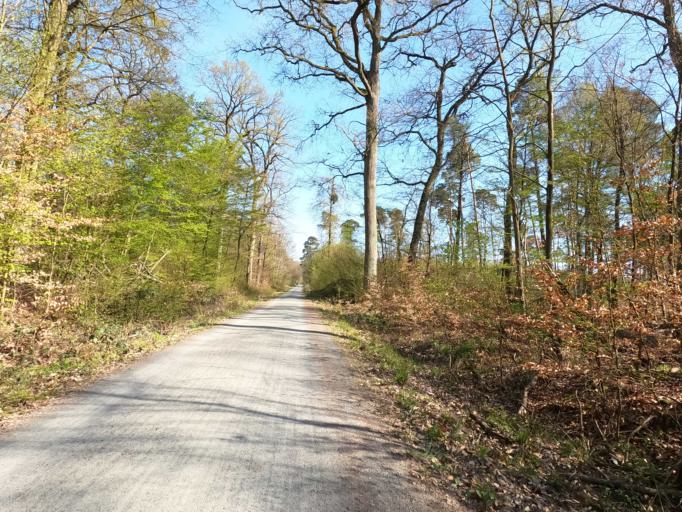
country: DE
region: Hesse
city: Langen
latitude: 50.0137
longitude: 8.6475
